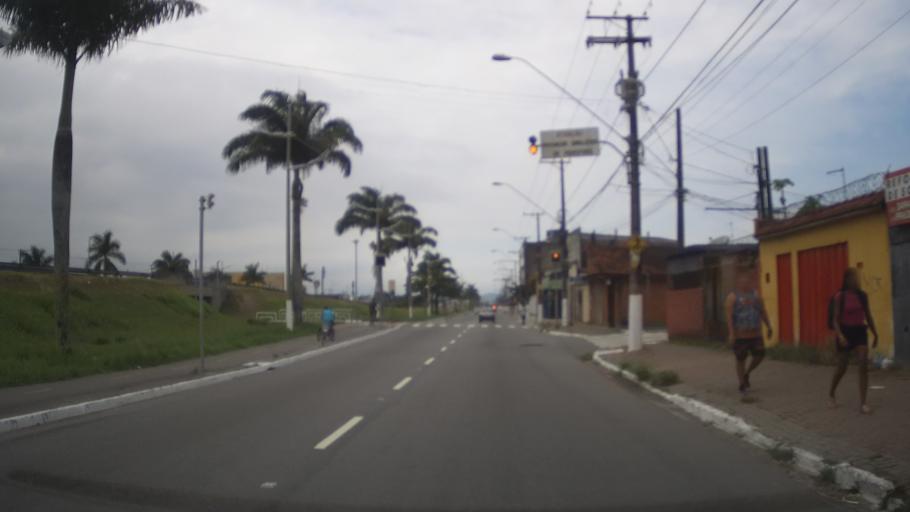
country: BR
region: Sao Paulo
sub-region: Praia Grande
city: Praia Grande
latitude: -24.0246
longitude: -46.4897
